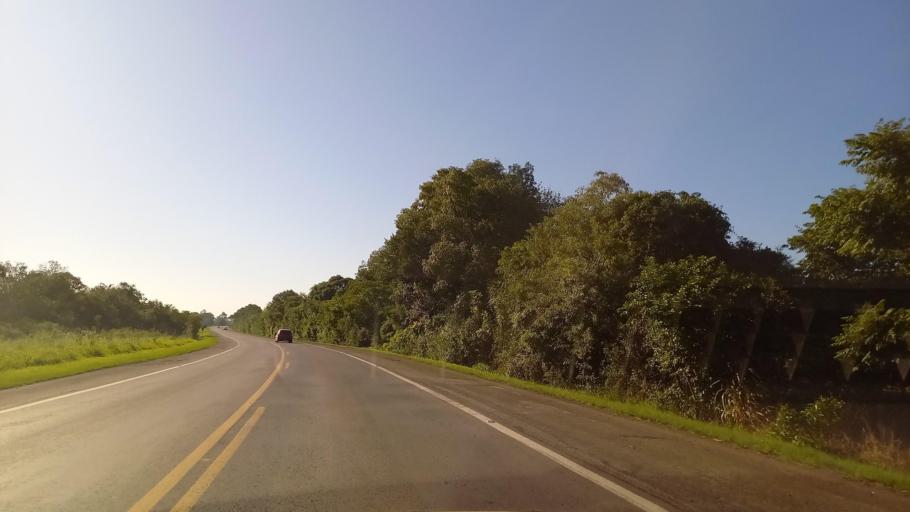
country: BR
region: Rio Grande do Sul
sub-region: Venancio Aires
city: Venancio Aires
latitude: -29.6693
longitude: -52.0370
